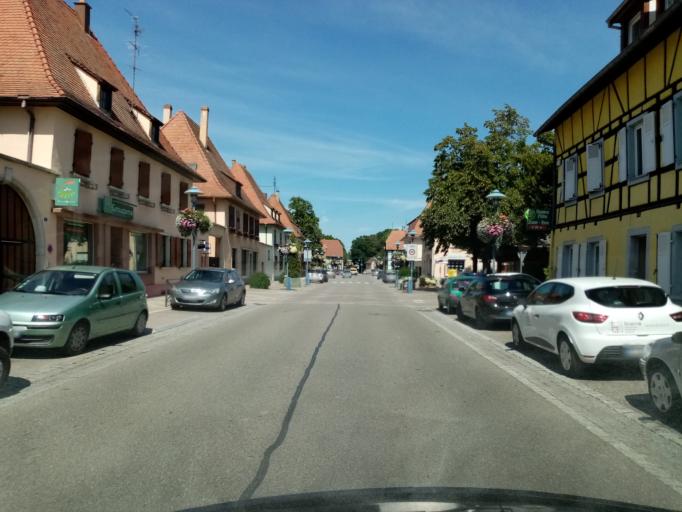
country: FR
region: Alsace
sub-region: Departement du Bas-Rhin
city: Marckolsheim
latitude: 48.1663
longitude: 7.5446
